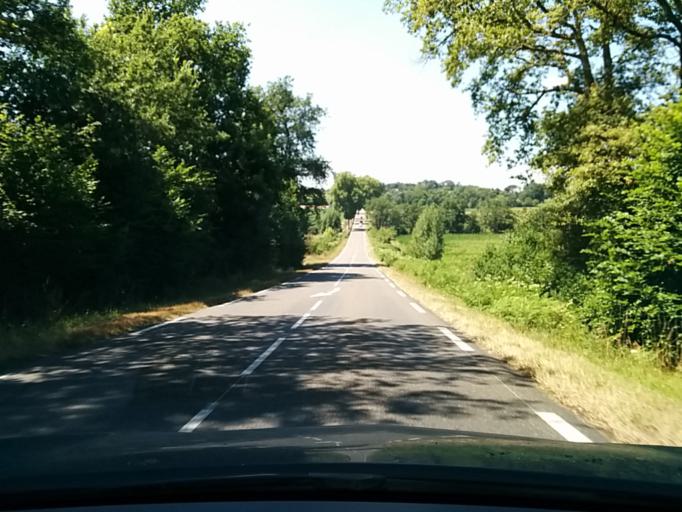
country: FR
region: Midi-Pyrenees
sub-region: Departement du Gers
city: Le Houga
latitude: 43.7712
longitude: -0.1272
